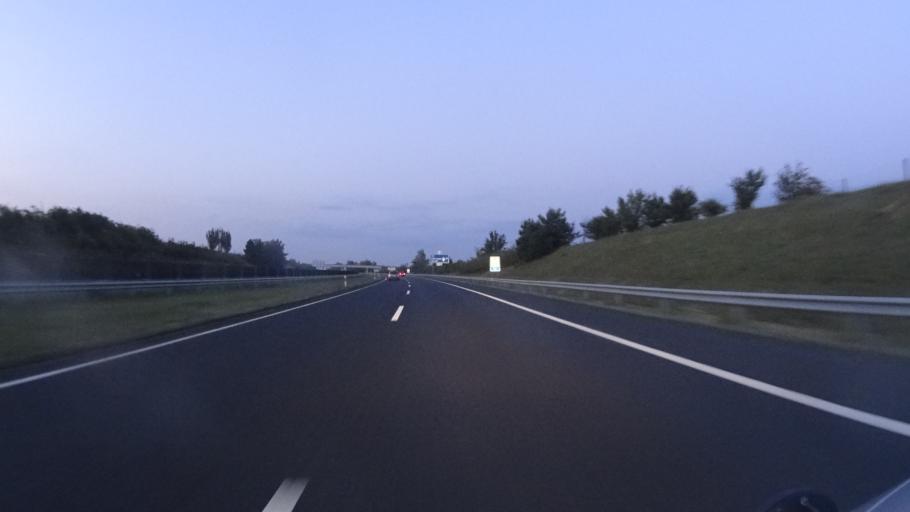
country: HU
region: Zala
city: Murakeresztur
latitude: 46.4506
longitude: 16.8748
